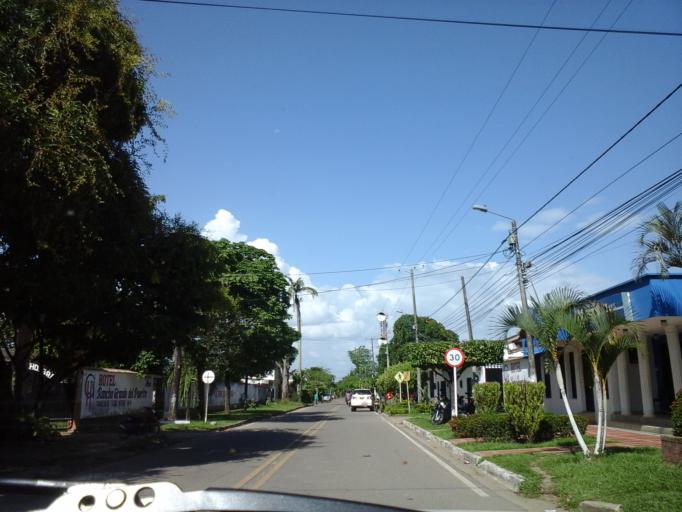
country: CO
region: Meta
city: Puerto Lopez
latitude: 4.0865
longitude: -72.9567
